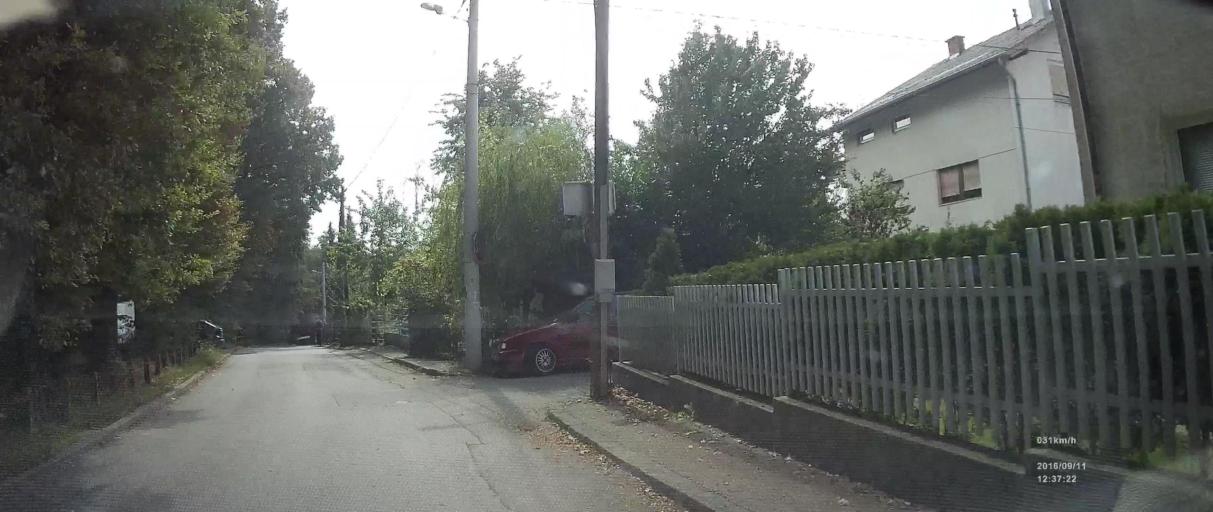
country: HR
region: Grad Zagreb
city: Zagreb
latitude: 45.8317
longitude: 16.0145
